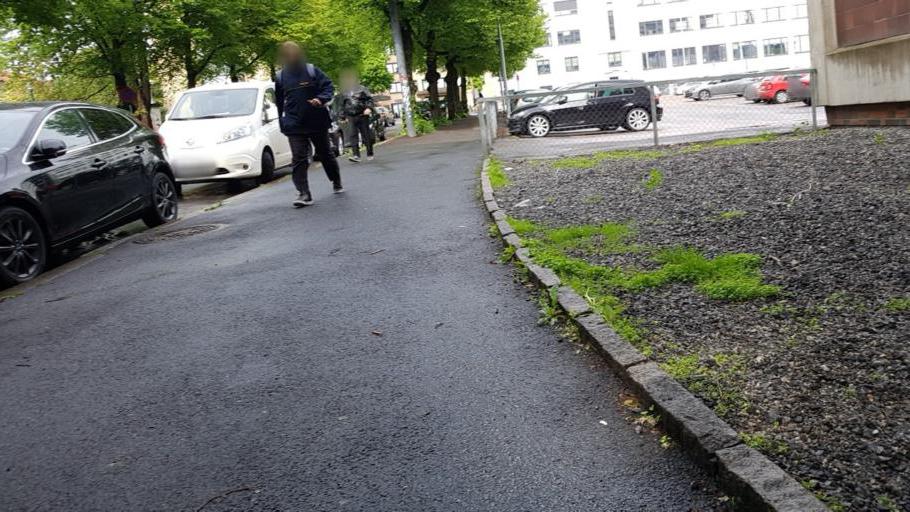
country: NO
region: Oslo
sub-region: Oslo
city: Oslo
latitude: 59.9262
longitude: 10.7658
